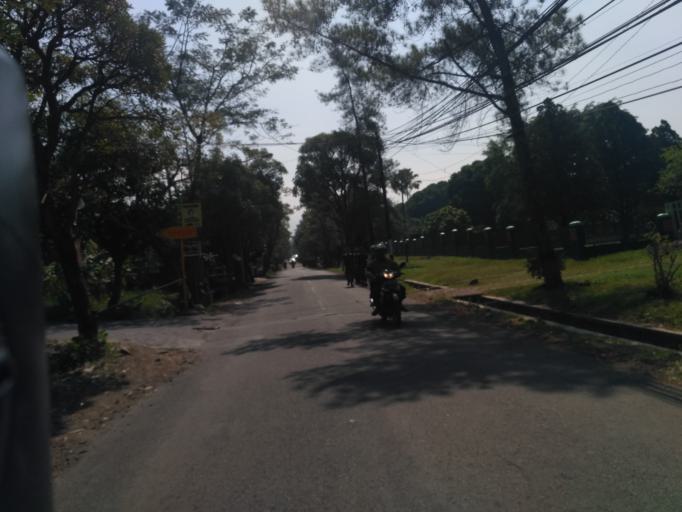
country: ID
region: East Java
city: Batu
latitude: -7.9012
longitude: 112.5813
